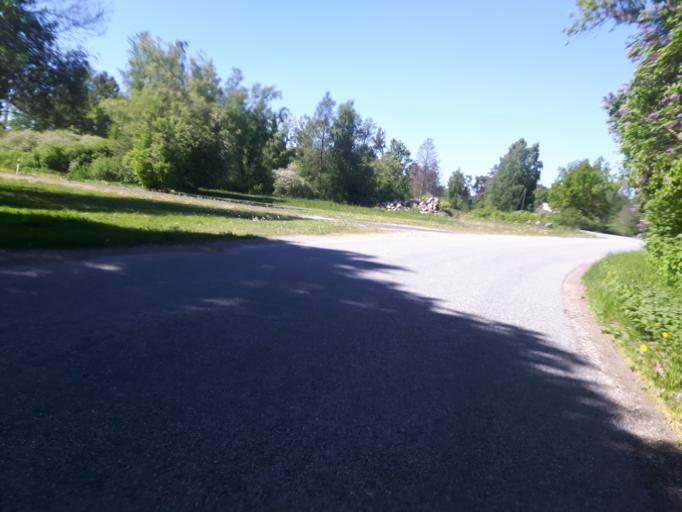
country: EE
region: Laeaene-Virumaa
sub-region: Haljala vald
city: Haljala
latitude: 59.5670
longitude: 26.2996
